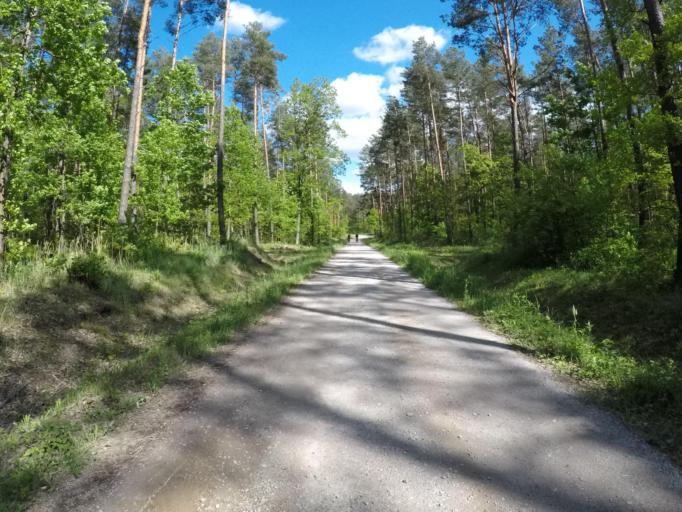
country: PL
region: Swietokrzyskie
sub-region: Powiat kielecki
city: Miedziana Gora
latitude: 50.9035
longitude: 20.5279
